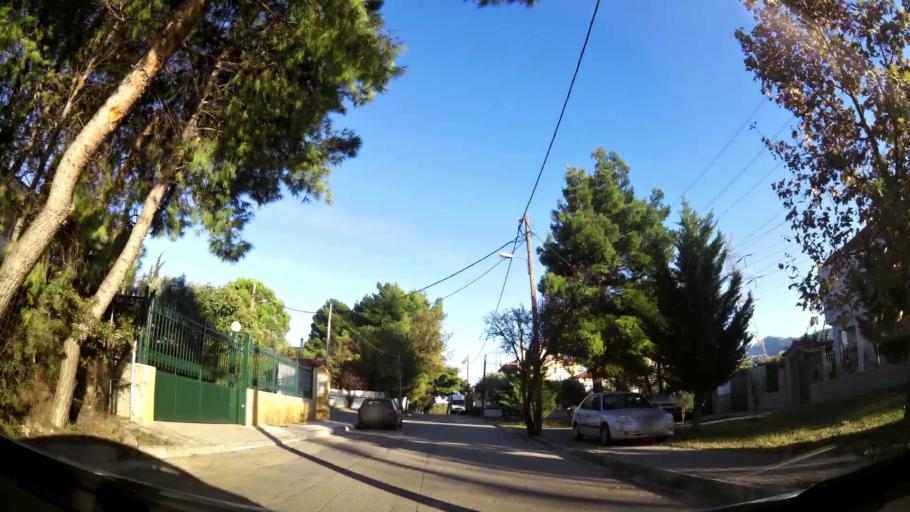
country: GR
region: Attica
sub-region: Nomarchia Anatolikis Attikis
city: Kryoneri
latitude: 38.1348
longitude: 23.8311
